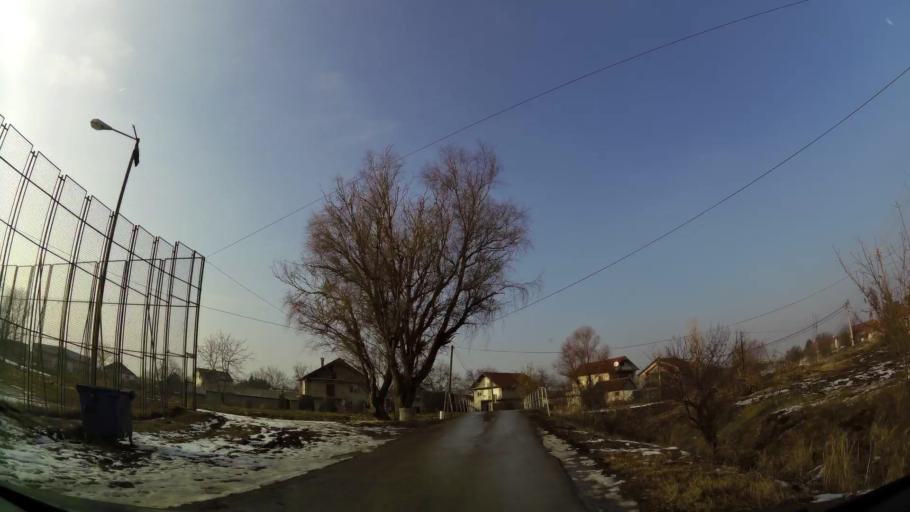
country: MK
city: Miladinovci
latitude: 41.9793
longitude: 21.6498
